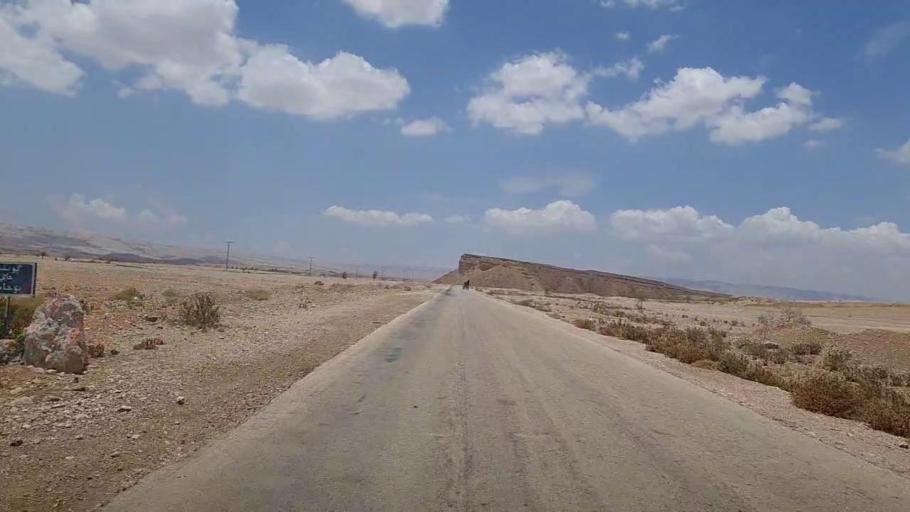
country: PK
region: Sindh
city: Sehwan
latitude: 26.3242
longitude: 67.6612
